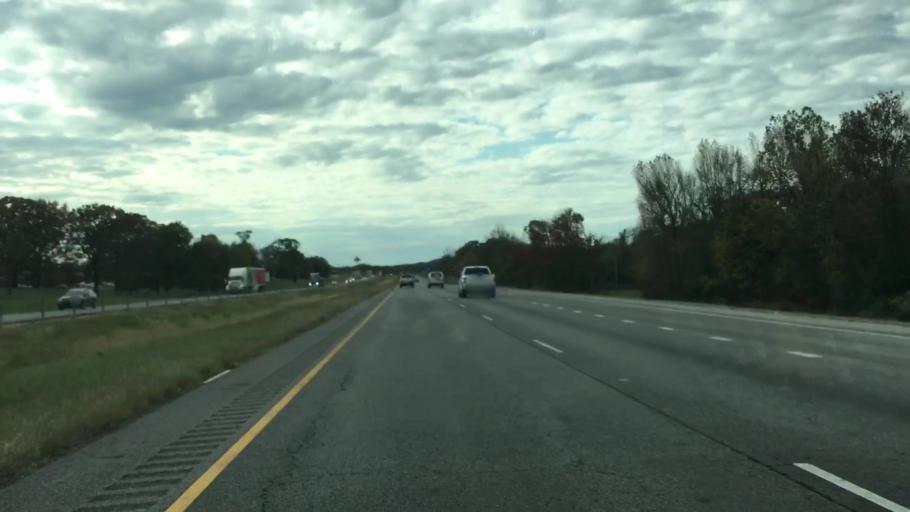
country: US
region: Arkansas
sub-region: Conway County
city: Morrilton
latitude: 35.1743
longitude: -92.7239
